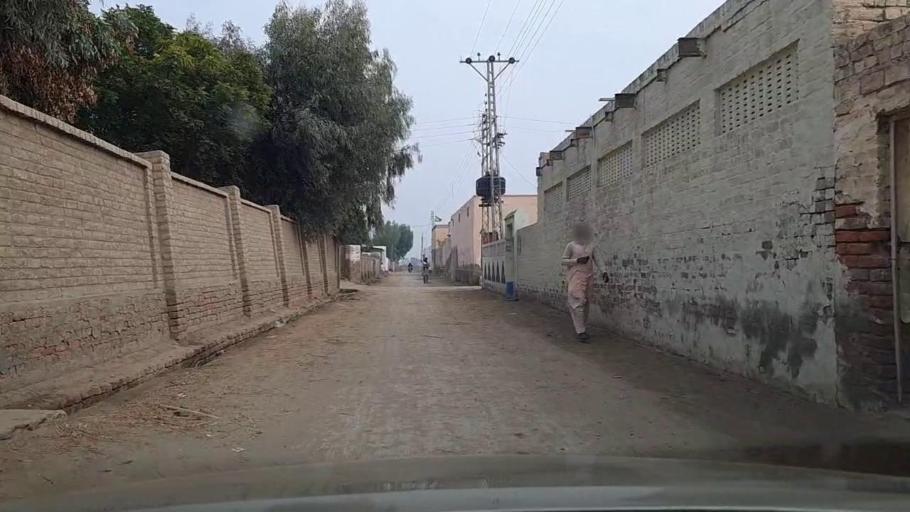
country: PK
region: Sindh
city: Sanghar
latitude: 26.1403
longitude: 68.9654
